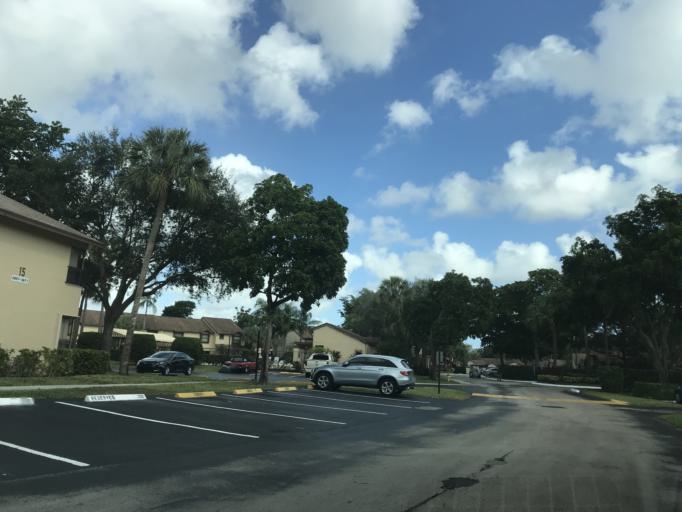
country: US
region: Florida
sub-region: Broward County
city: Coconut Creek
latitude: 26.2690
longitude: -80.1908
